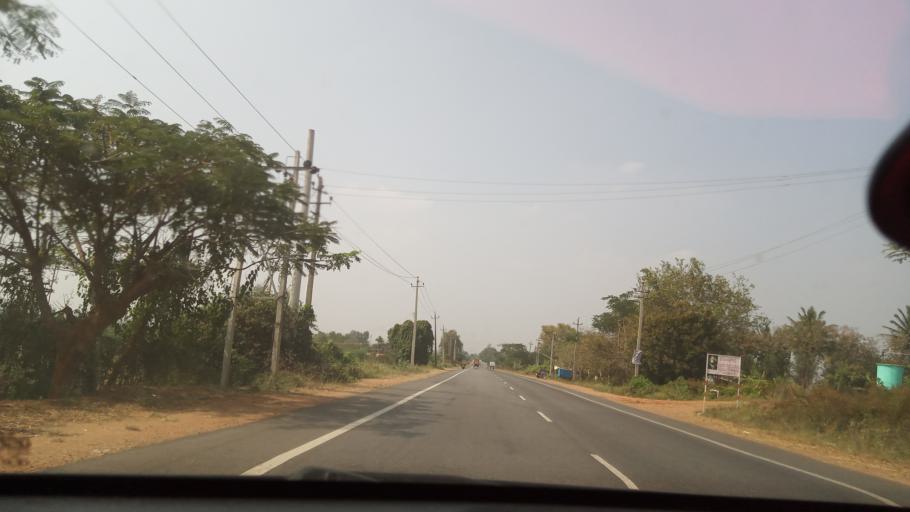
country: IN
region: Karnataka
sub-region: Mysore
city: Nanjangud
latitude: 12.0950
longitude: 76.7206
